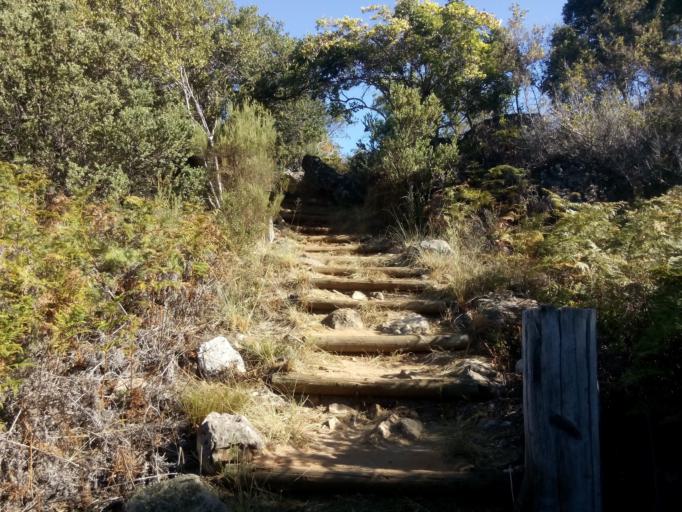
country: ZA
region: Western Cape
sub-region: City of Cape Town
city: Newlands
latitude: -33.9878
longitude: 18.4260
